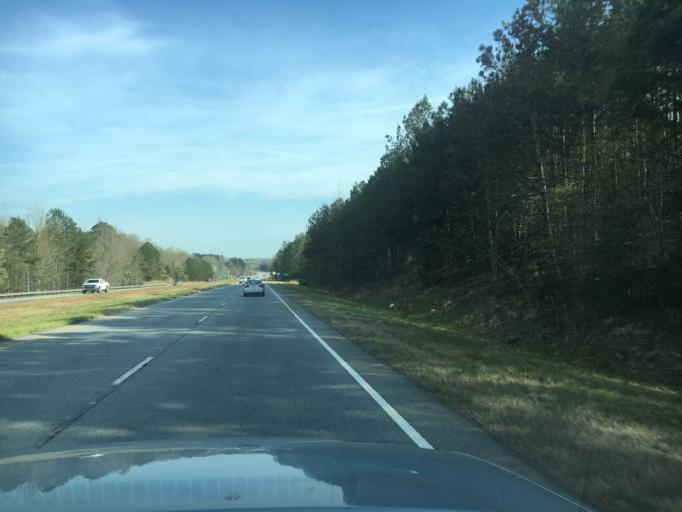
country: US
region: Georgia
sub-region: Stephens County
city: Toccoa
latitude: 34.5492
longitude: -83.3694
